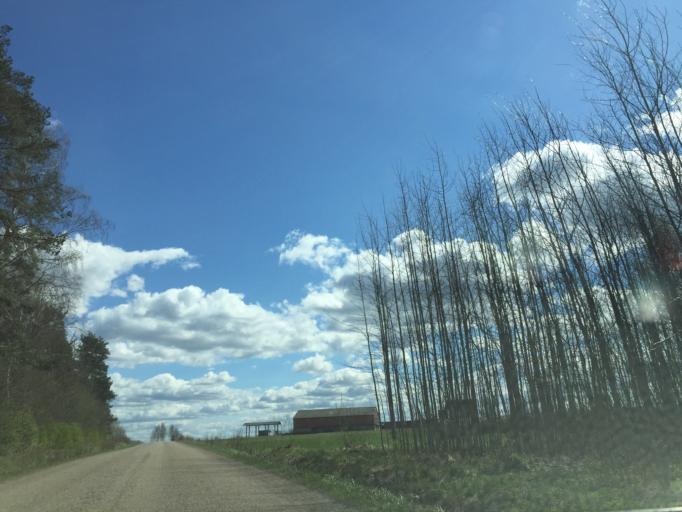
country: LV
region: Rezekne
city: Rezekne
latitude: 56.5759
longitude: 27.1323
